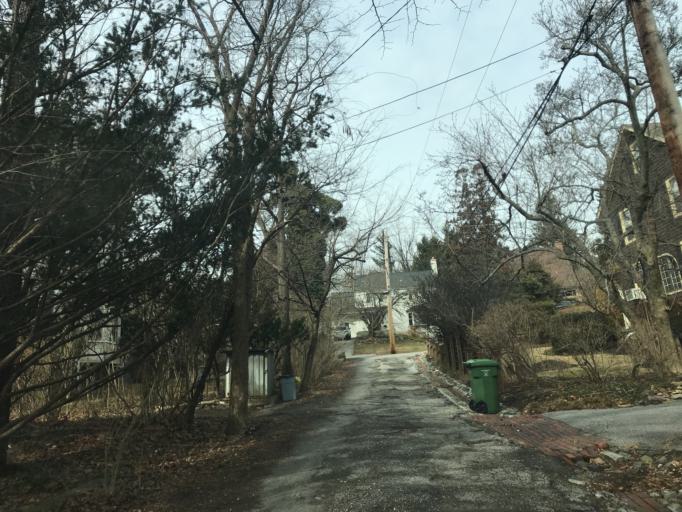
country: US
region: Maryland
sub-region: Baltimore County
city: Pikesville
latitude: 39.3630
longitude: -76.6581
